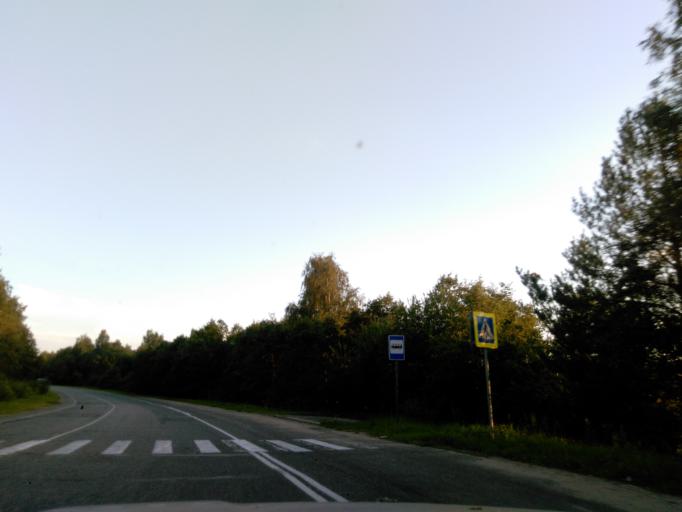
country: RU
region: Tverskaya
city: Konakovo
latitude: 56.6516
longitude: 36.7089
